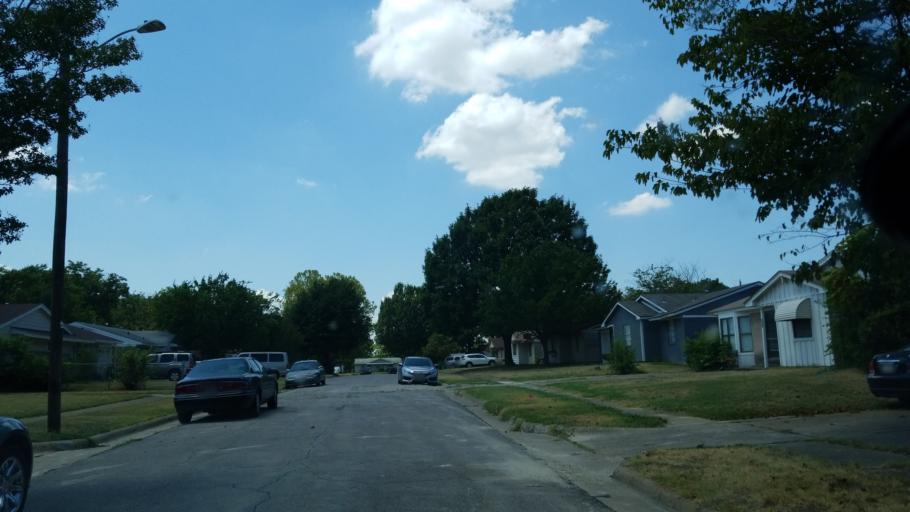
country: US
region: Texas
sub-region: Dallas County
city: Duncanville
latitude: 32.6716
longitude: -96.8993
